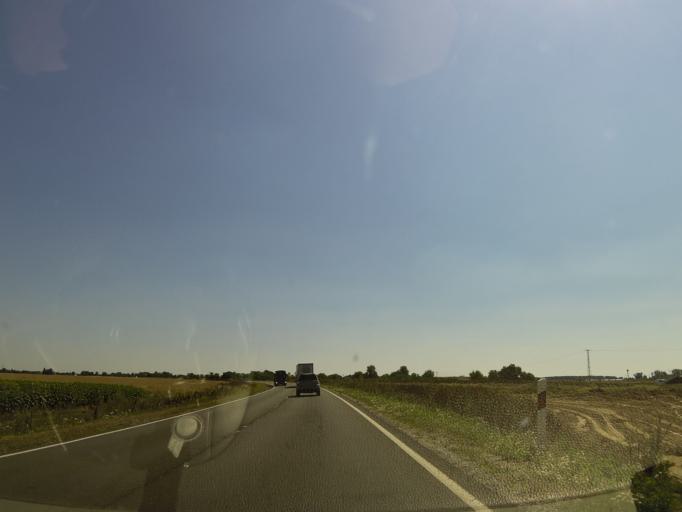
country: HU
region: Jasz-Nagykun-Szolnok
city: Torokszentmiklos
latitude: 47.1911
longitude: 20.4552
